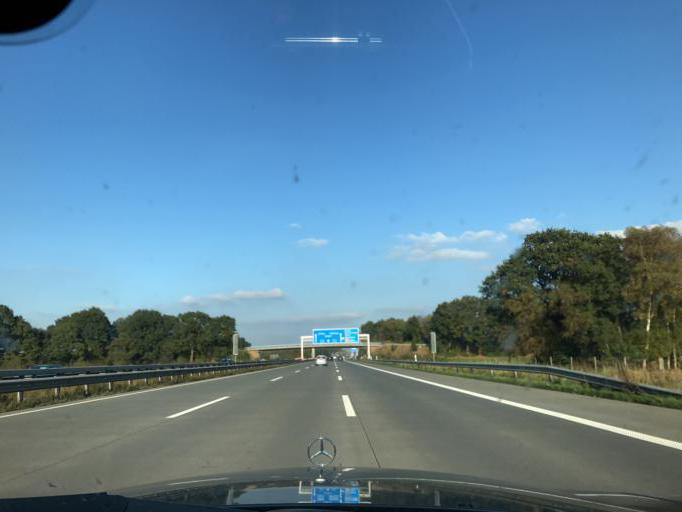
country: DE
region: Lower Saxony
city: Horstedt
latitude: 53.1865
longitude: 9.2748
